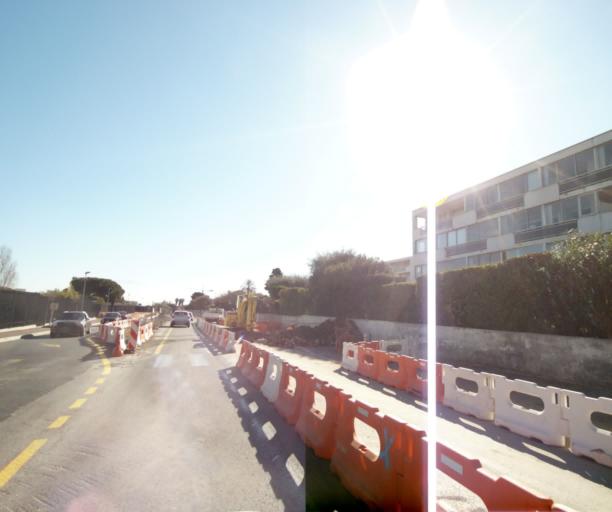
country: FR
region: Provence-Alpes-Cote d'Azur
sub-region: Departement des Alpes-Maritimes
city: Antibes
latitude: 43.5934
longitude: 7.1124
